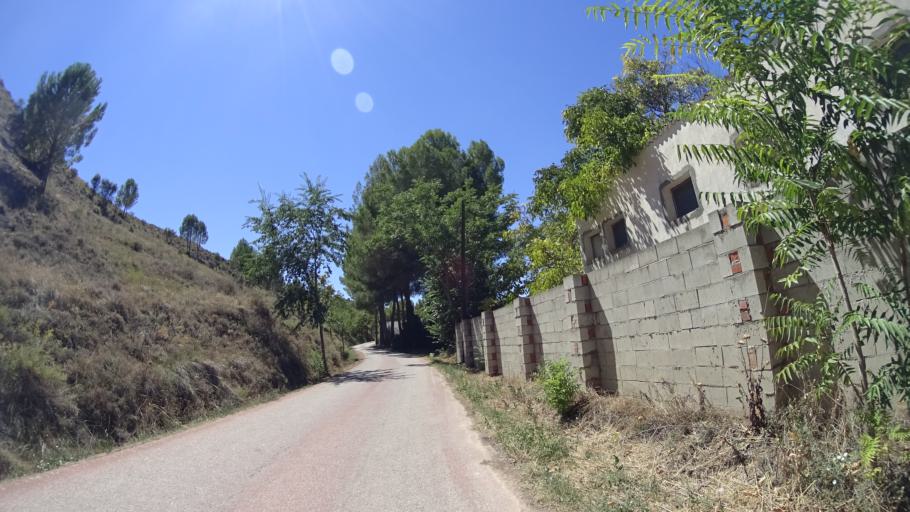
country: ES
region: Madrid
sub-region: Provincia de Madrid
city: Tielmes
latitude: 40.2400
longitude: -3.3058
